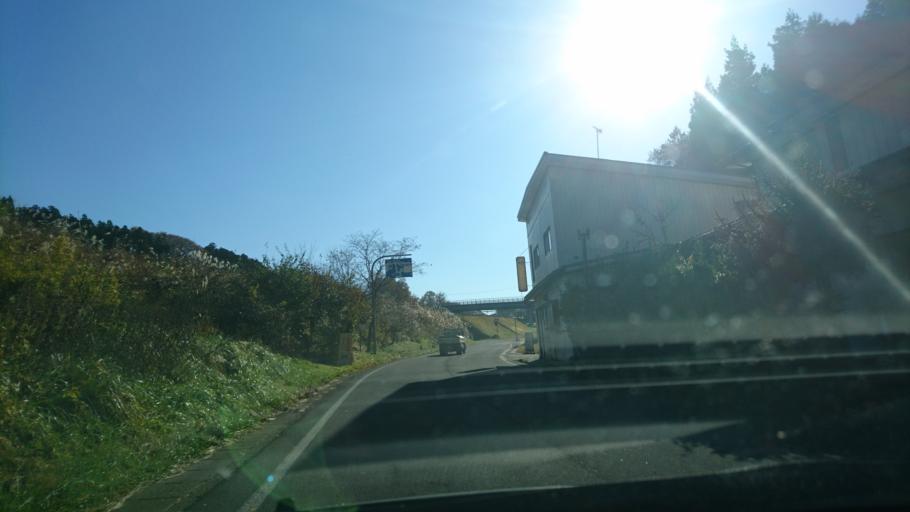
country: JP
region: Iwate
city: Ichinoseki
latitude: 39.0011
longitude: 141.2665
